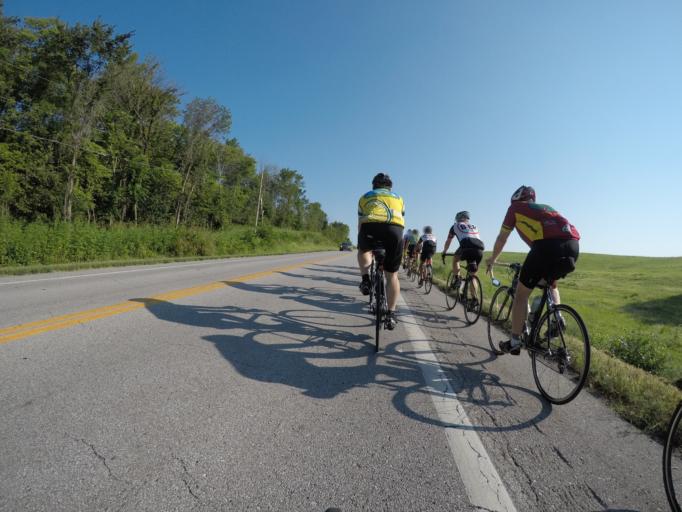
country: US
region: Missouri
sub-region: Platte County
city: Weston
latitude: 39.3890
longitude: -94.8641
